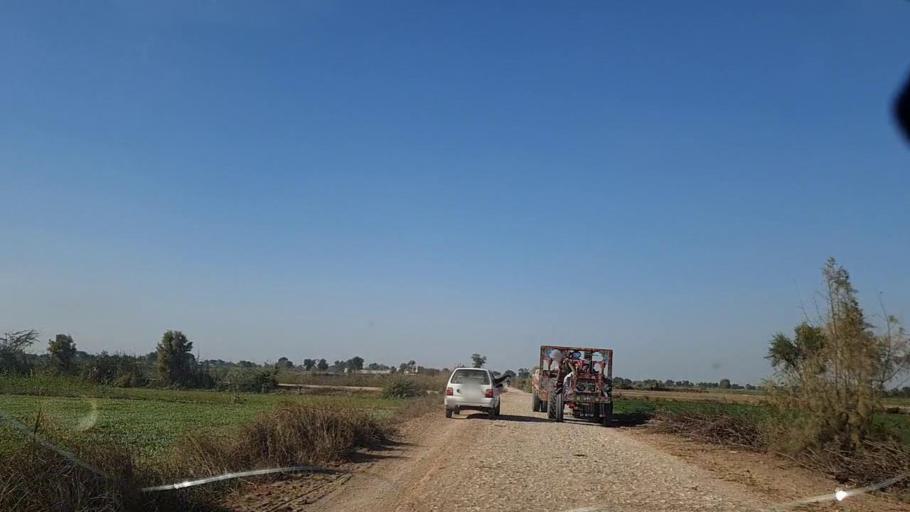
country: PK
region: Sindh
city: Khanpur
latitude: 27.7813
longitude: 69.3557
